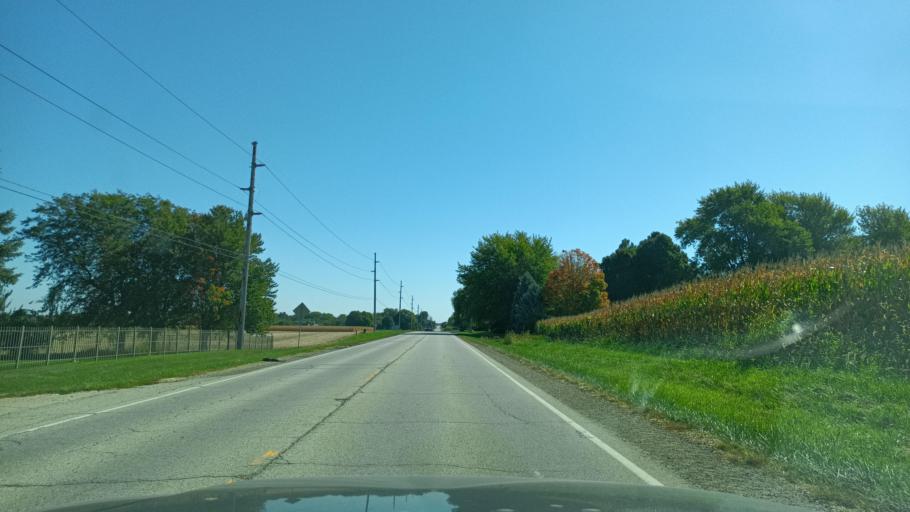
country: US
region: Illinois
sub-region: Peoria County
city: Dunlap
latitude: 40.7856
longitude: -89.7259
